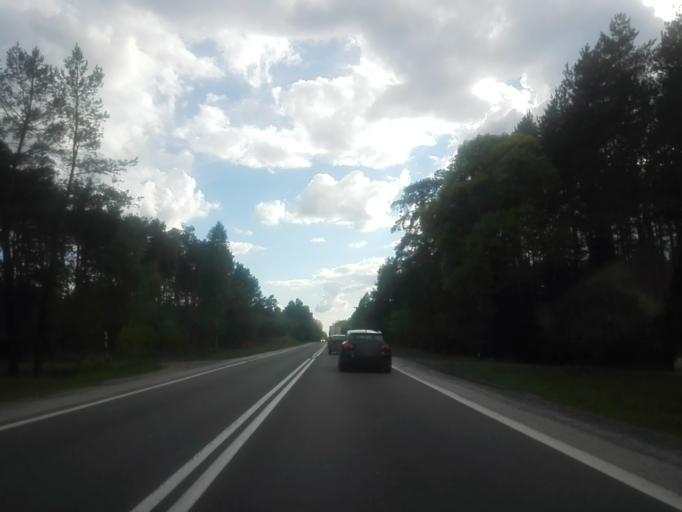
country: PL
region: Masovian Voivodeship
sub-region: Powiat ostrowski
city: Brok
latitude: 52.7272
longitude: 21.7265
